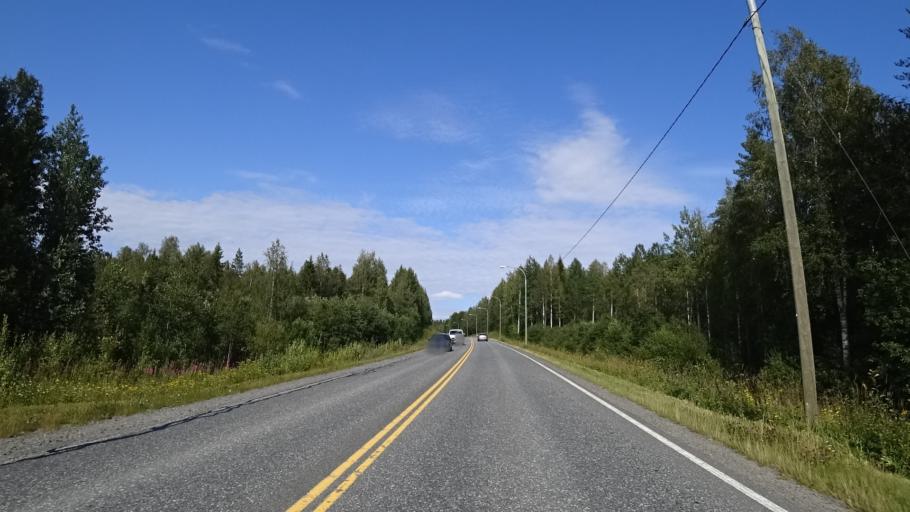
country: FI
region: North Karelia
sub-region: Joensuu
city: Eno
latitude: 62.7807
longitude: 30.0722
